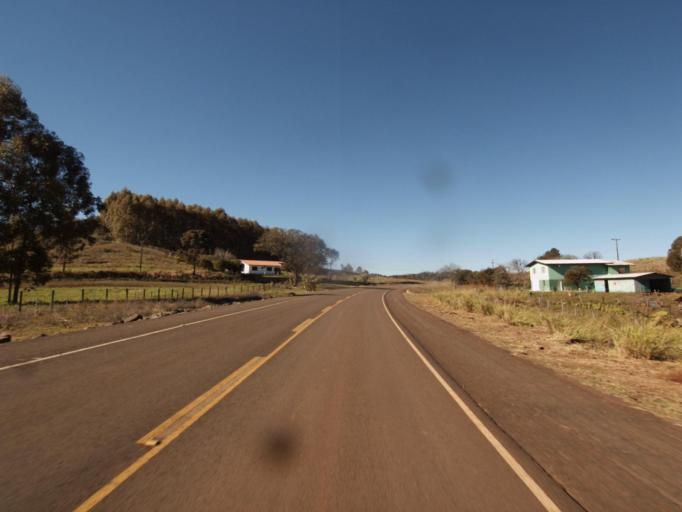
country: AR
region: Misiones
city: Bernardo de Irigoyen
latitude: -26.6133
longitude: -53.6825
